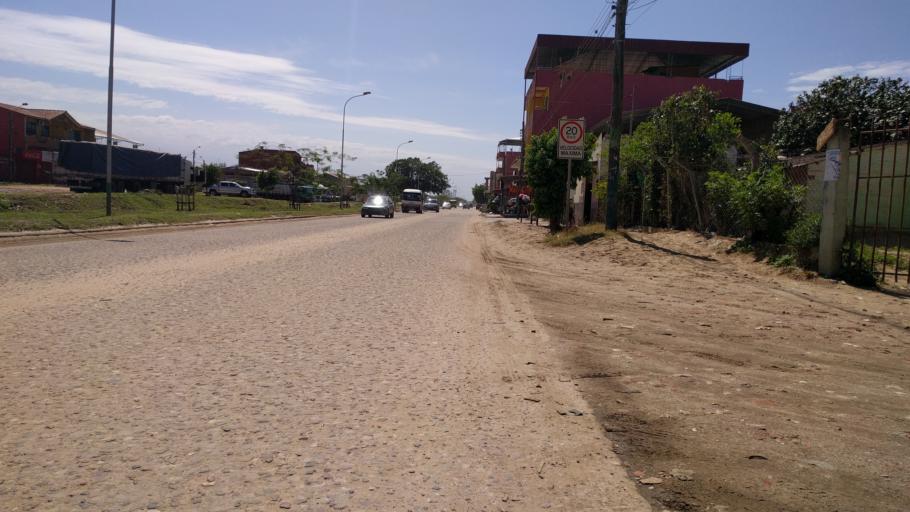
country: BO
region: Santa Cruz
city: Santa Cruz de la Sierra
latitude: -17.8208
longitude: -63.2293
